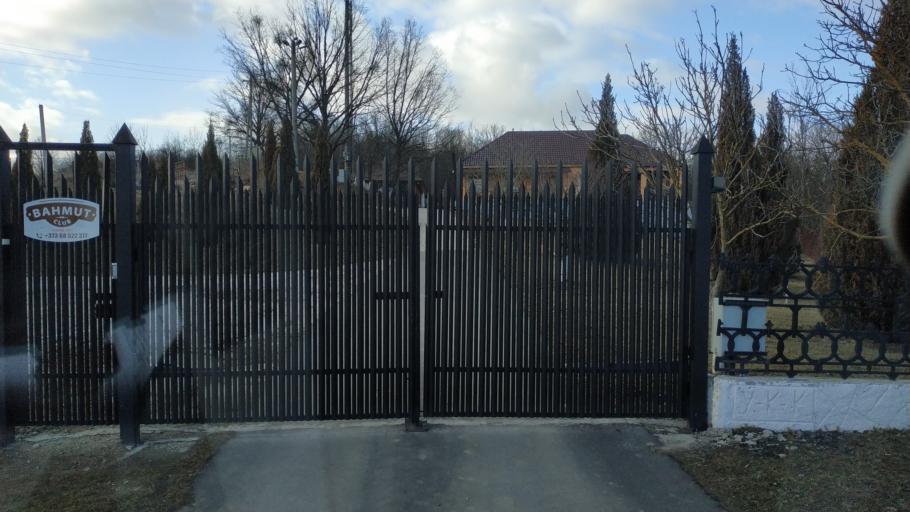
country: MD
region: Calarasi
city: Calarasi
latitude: 47.3319
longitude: 28.0888
